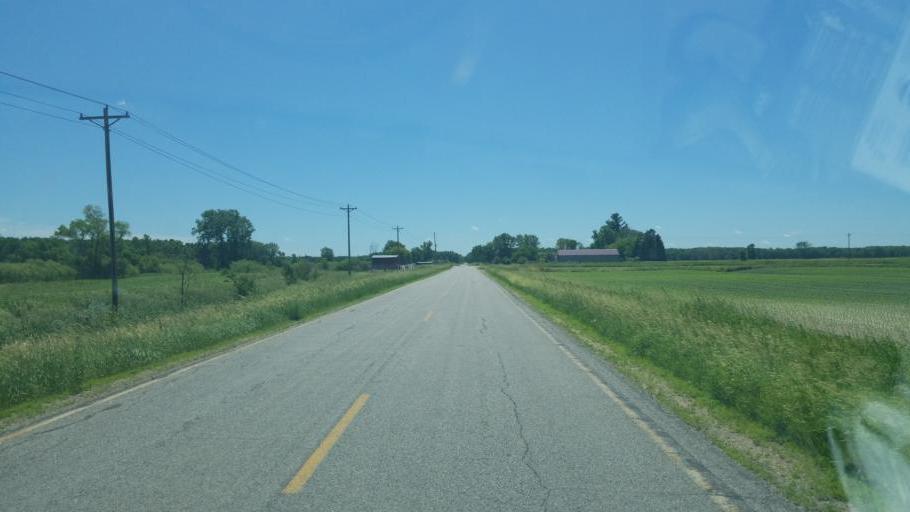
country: US
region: Wisconsin
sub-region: Juneau County
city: New Lisbon
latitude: 44.0052
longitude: -90.2718
